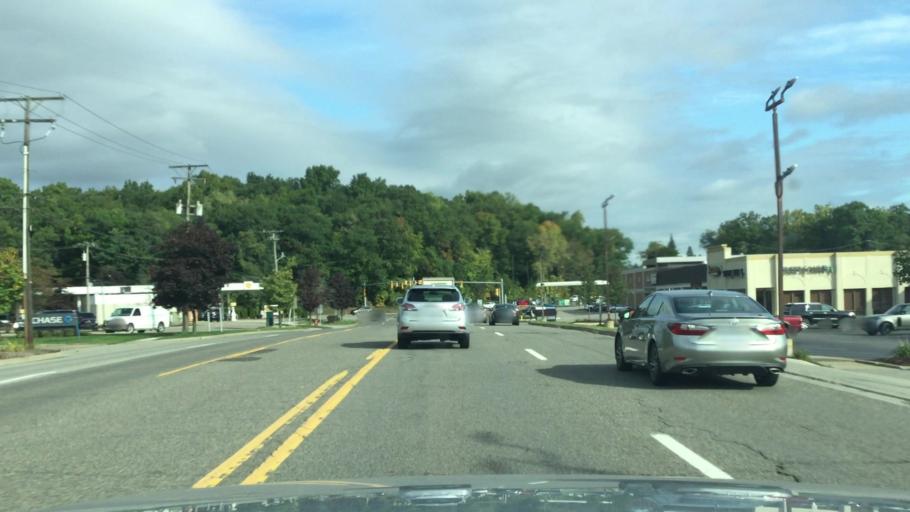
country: US
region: Michigan
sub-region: Oakland County
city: Orchard Lake
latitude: 42.5773
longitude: -83.3623
